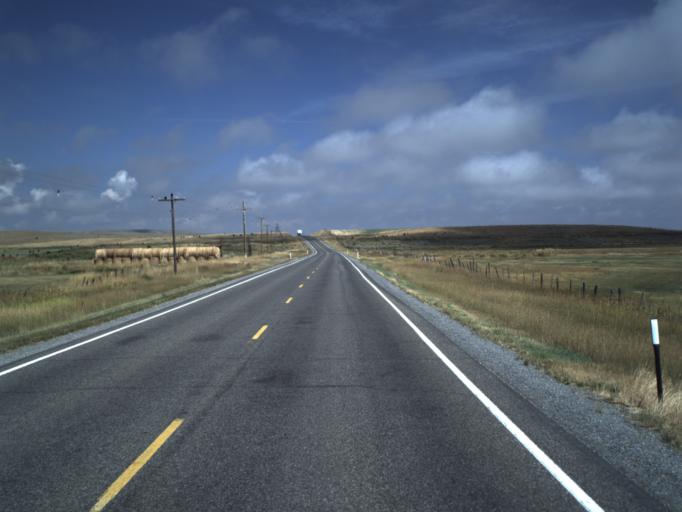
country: US
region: Utah
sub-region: Rich County
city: Randolph
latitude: 41.7224
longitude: -111.1592
